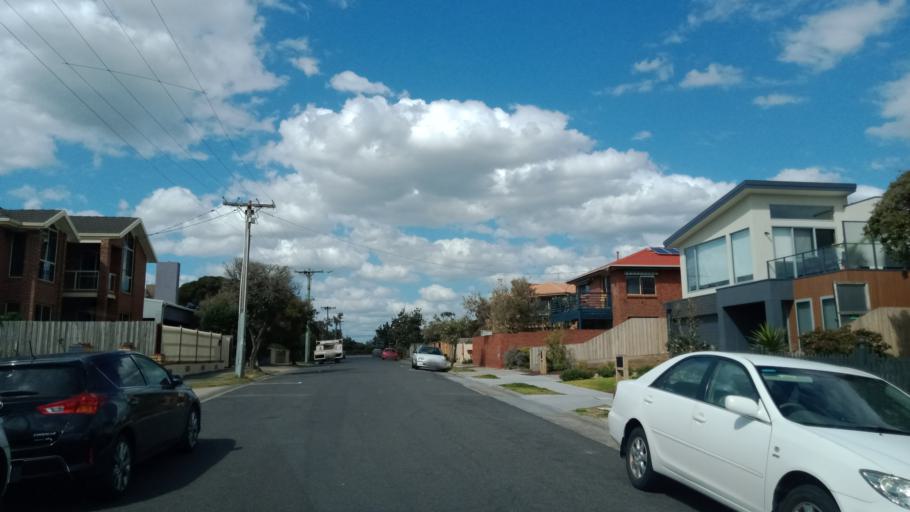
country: AU
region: Victoria
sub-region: Kingston
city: Chelsea
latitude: -38.0572
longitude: 145.1159
